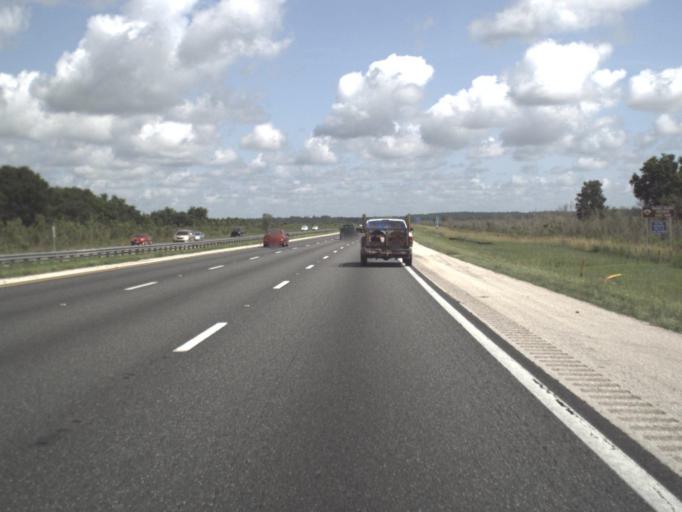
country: US
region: Florida
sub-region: Alachua County
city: Gainesville
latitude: 29.5577
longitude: -82.3439
